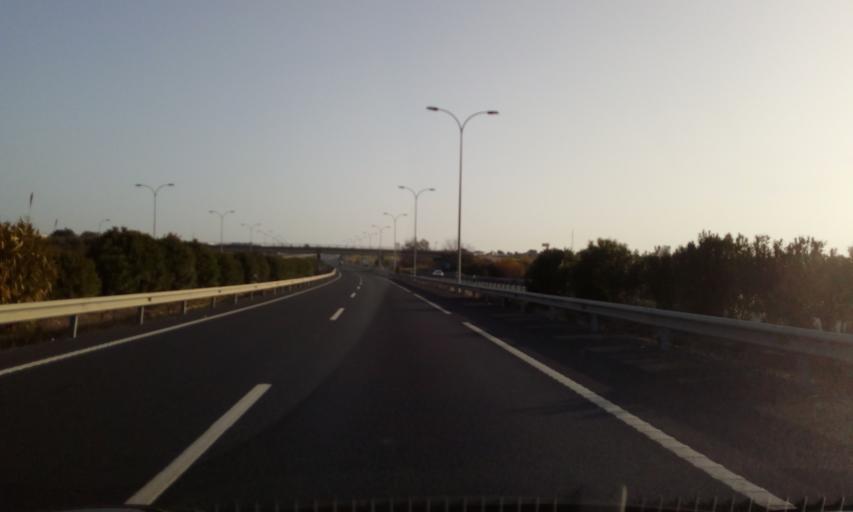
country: ES
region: Andalusia
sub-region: Provincia de Huelva
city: Bollullos par del Condado
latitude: 37.3545
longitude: -6.5579
